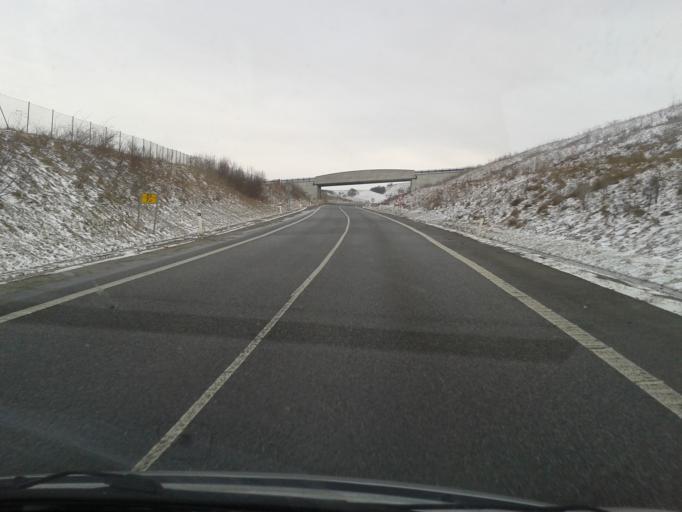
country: SK
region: Zilinsky
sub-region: Okres Zilina
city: Trstena
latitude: 49.3545
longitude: 19.6199
